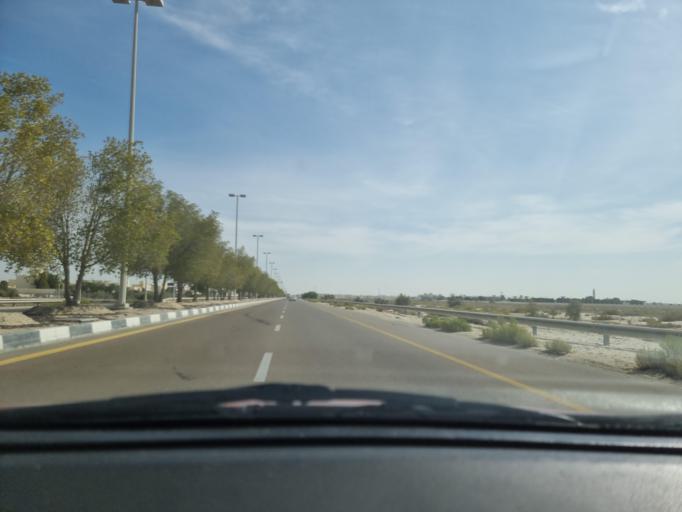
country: AE
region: Abu Dhabi
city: Abu Dhabi
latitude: 24.3842
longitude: 54.6830
